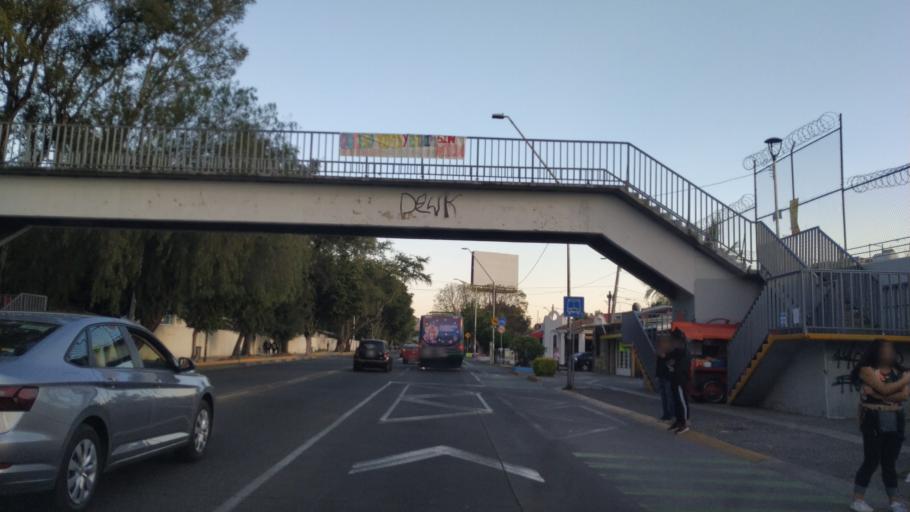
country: MX
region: Jalisco
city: Tlaquepaque
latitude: 20.6561
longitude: -103.3280
